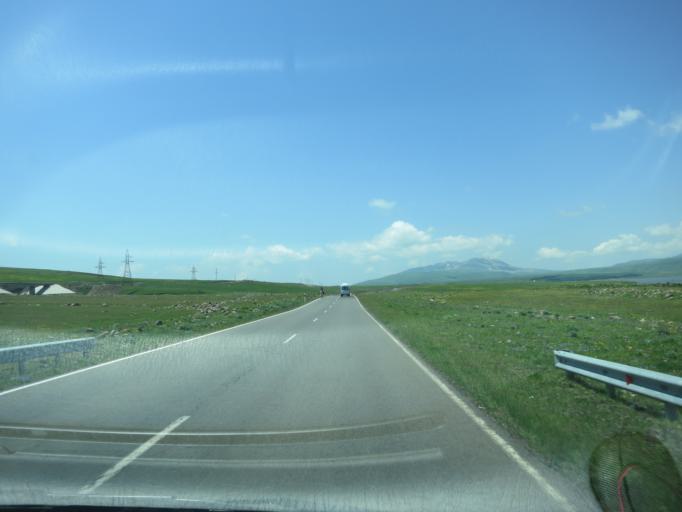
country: GE
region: Samtskhe-Javakheti
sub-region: Ninotsminda
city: Ninotsminda
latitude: 41.4100
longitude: 43.8253
